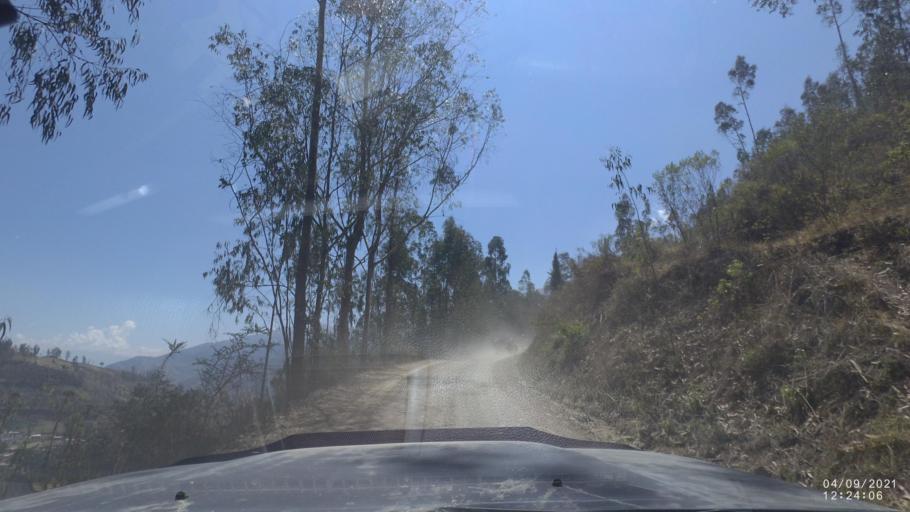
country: BO
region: Cochabamba
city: Colchani
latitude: -17.2361
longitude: -66.5259
